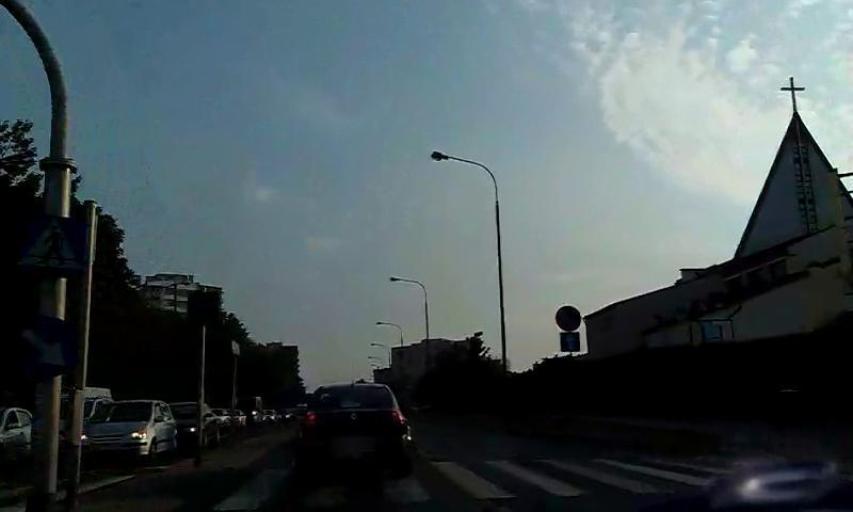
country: PL
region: Lublin Voivodeship
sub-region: Powiat lubelski
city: Lublin
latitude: 51.2342
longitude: 22.5935
